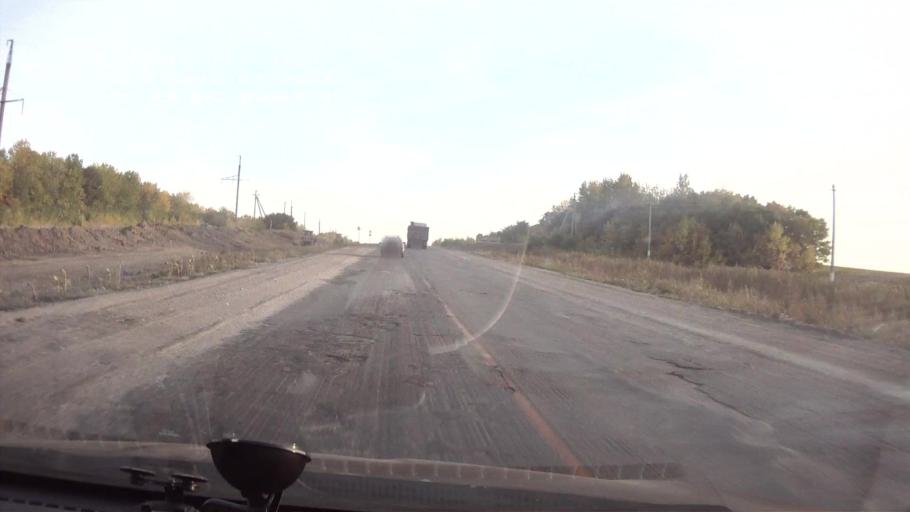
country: RU
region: Saratov
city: Krasnoarmeysk
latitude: 51.1909
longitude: 45.6481
